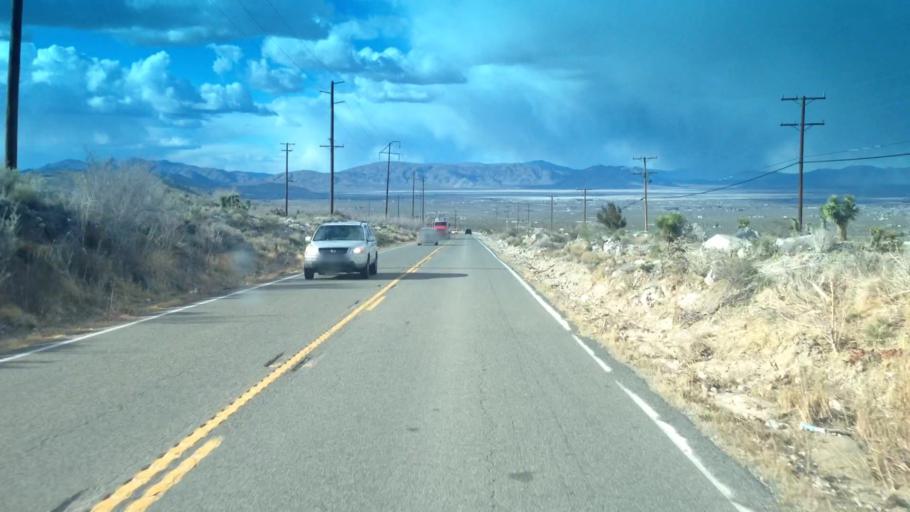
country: US
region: California
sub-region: San Bernardino County
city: Lucerne Valley
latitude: 34.3808
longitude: -116.8701
